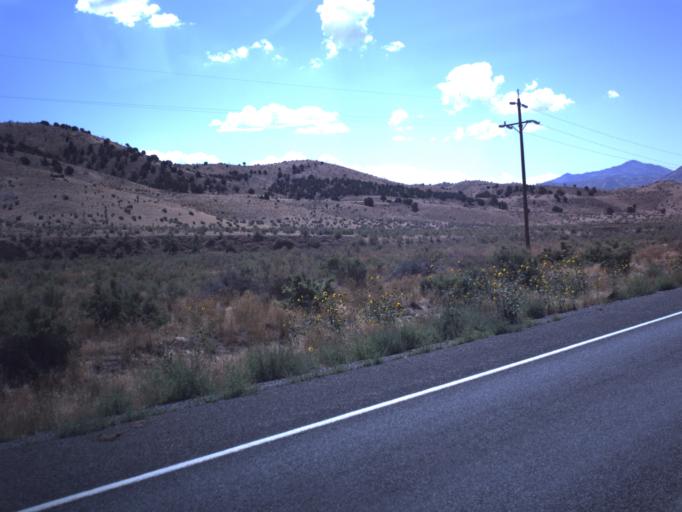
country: US
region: Utah
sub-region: Juab County
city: Nephi
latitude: 39.6141
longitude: -112.1316
